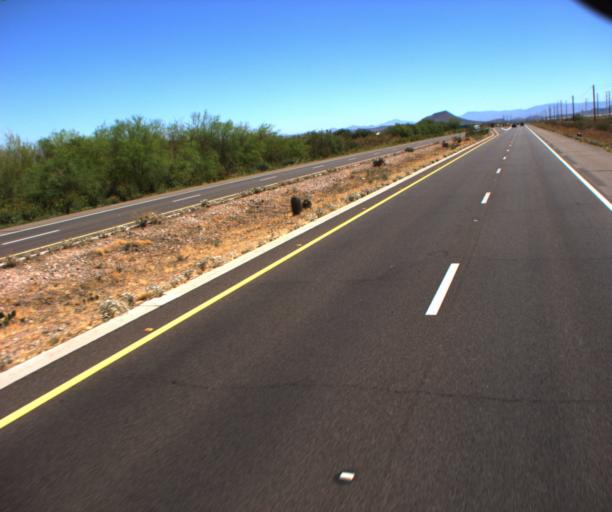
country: US
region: Arizona
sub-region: Maricopa County
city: Mesa
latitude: 33.4822
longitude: -111.8244
